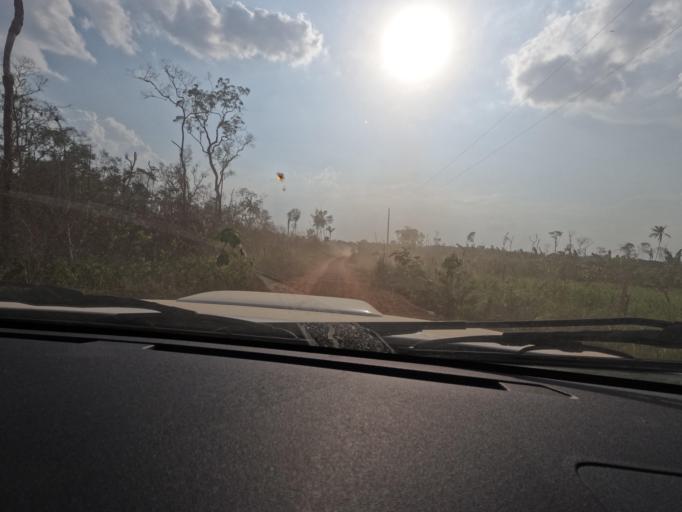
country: BR
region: Rondonia
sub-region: Porto Velho
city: Porto Velho
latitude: -8.5739
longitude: -64.0087
